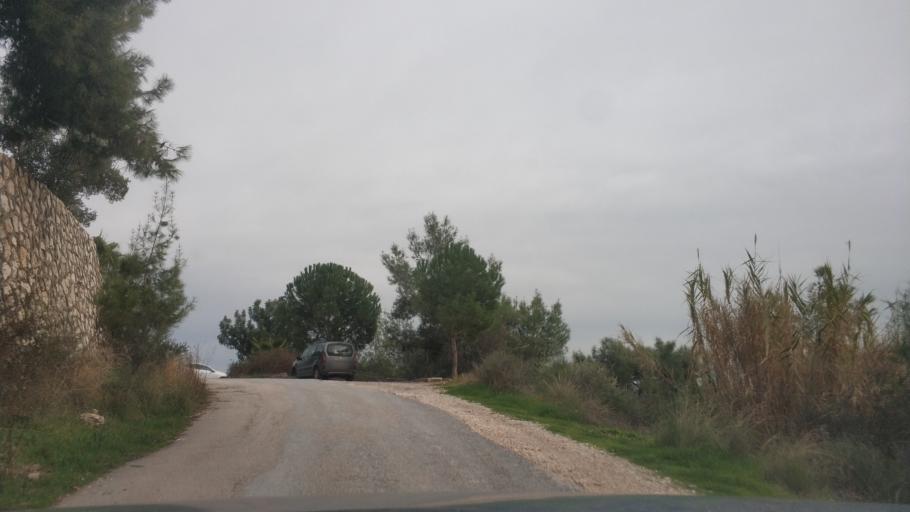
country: TR
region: Adana
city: Adana
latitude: 37.0990
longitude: 35.2901
